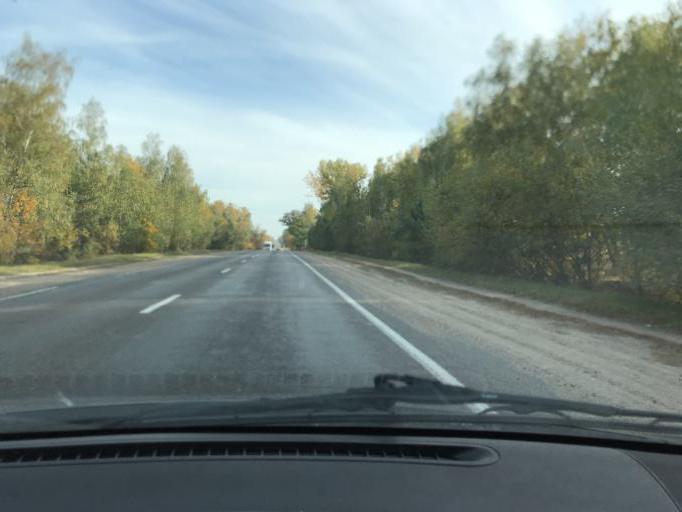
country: BY
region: Brest
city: Lahishyn
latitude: 52.2305
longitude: 26.0182
